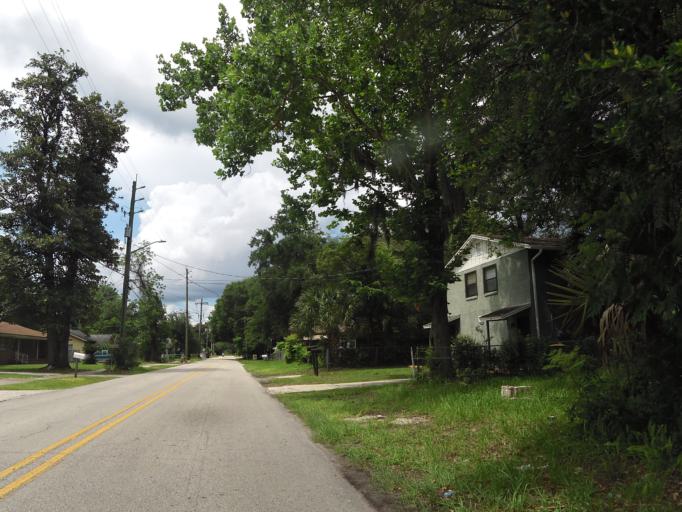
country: US
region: Florida
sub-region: Duval County
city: Jacksonville
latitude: 30.3836
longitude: -81.6411
